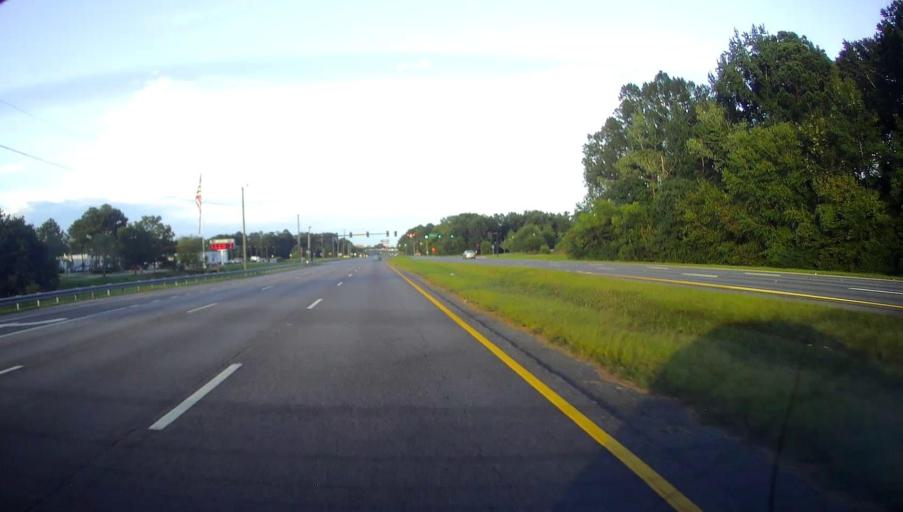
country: US
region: Georgia
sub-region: Muscogee County
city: Columbus
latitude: 32.5081
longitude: -84.9379
